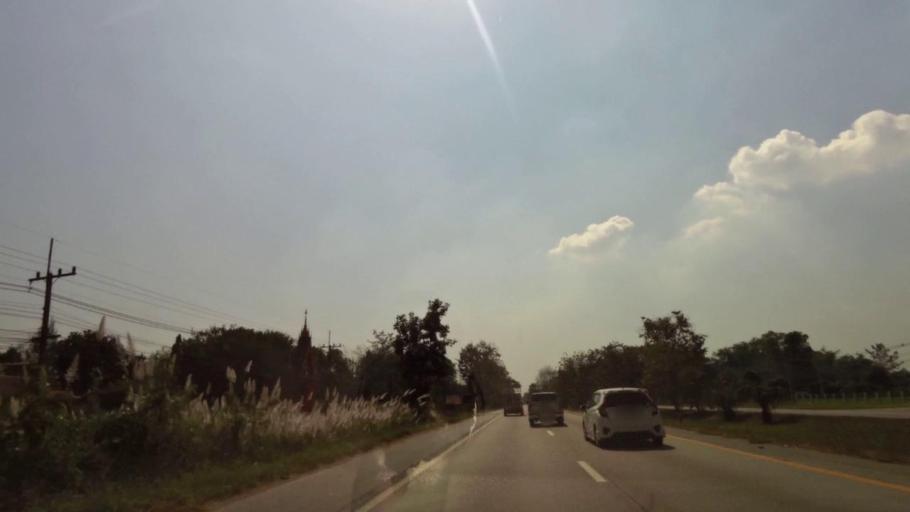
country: TH
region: Phichit
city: Wachira Barami
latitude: 16.5561
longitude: 100.1475
